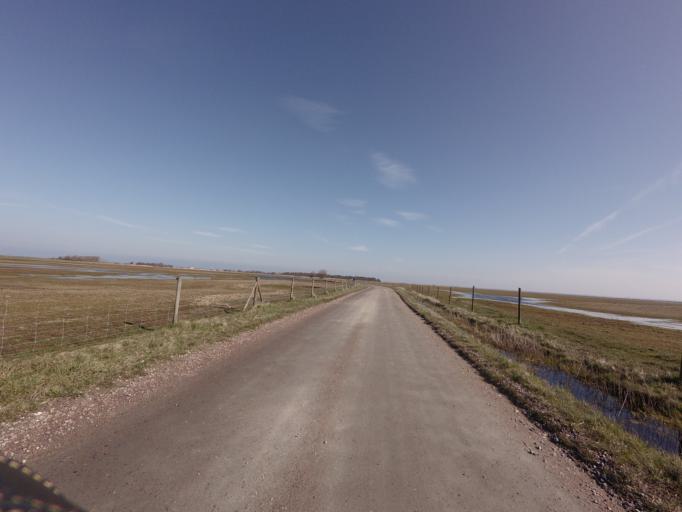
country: SE
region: Skane
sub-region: Vellinge Kommun
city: Skanor med Falsterbo
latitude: 55.4256
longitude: 12.8561
